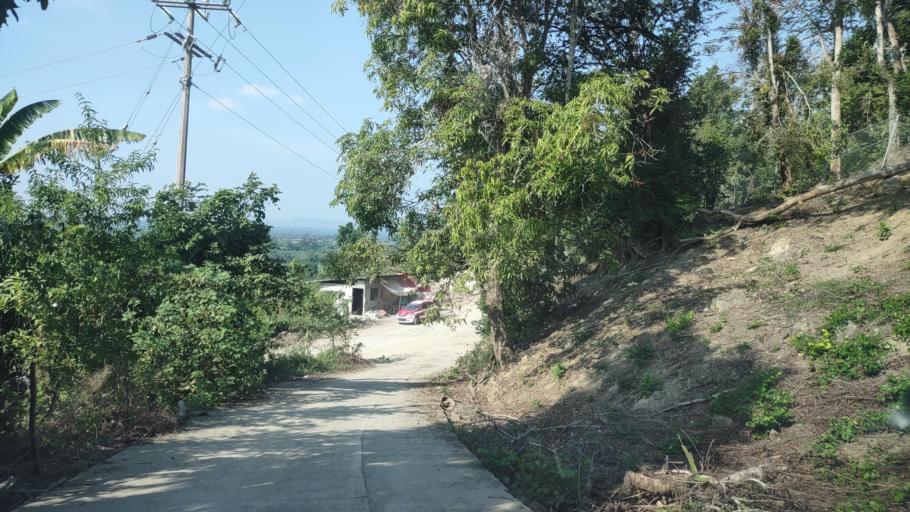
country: MX
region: Veracruz
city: Agua Dulce
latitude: 20.2958
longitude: -97.2827
